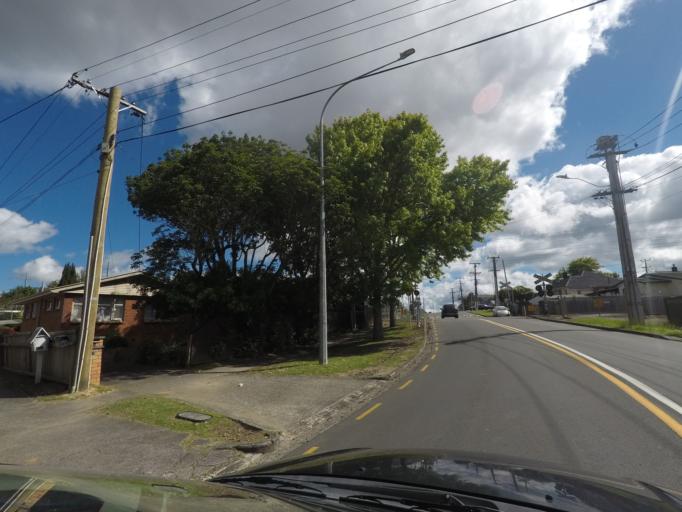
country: NZ
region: Auckland
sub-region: Auckland
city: Waitakere
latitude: -36.9114
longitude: 174.6681
